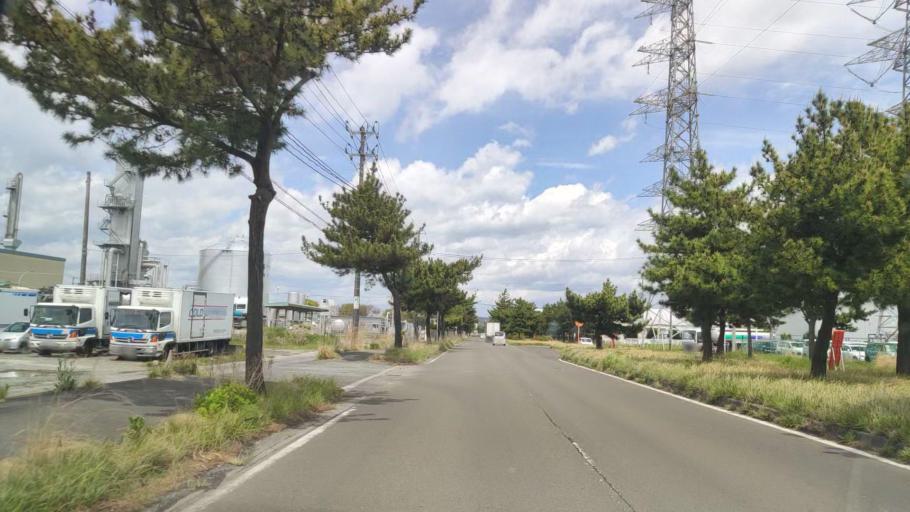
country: JP
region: Miyagi
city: Shiogama
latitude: 38.2853
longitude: 141.0245
